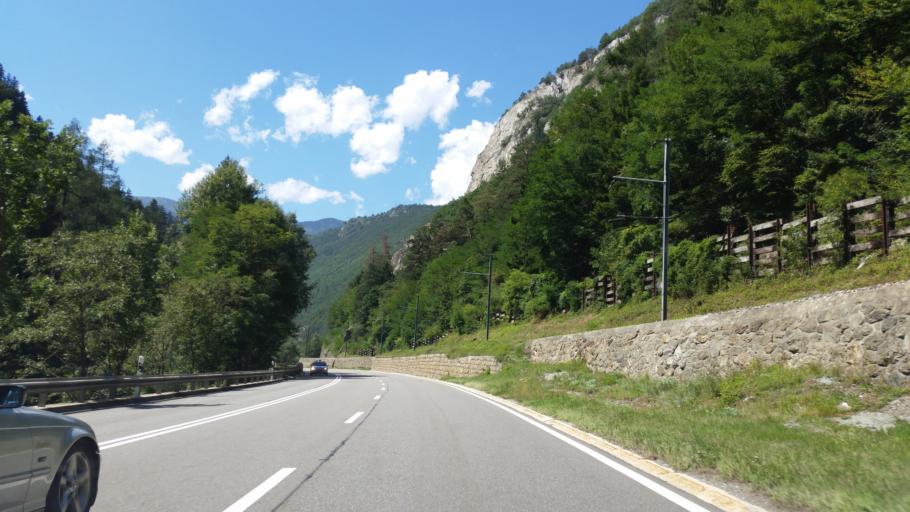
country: CH
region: Valais
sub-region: Martigny District
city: Martigny-Ville
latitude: 46.0811
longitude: 7.1115
